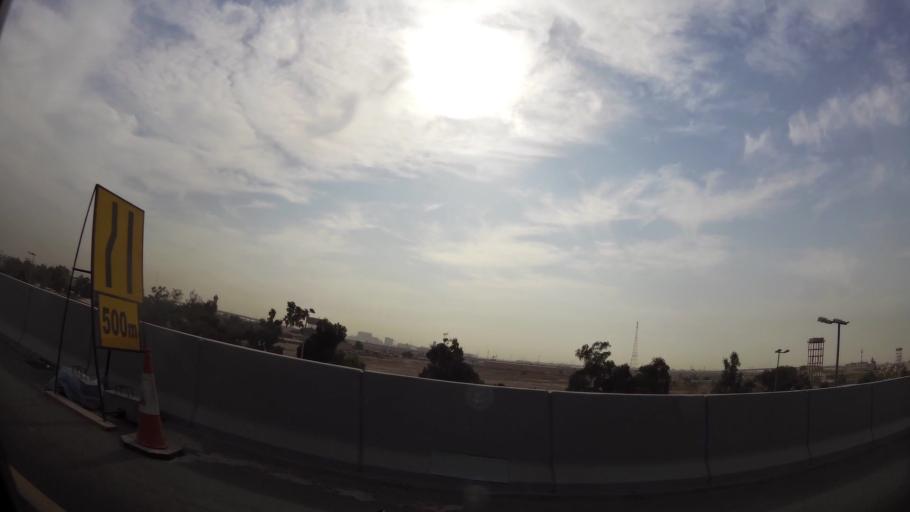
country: KW
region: Al Asimah
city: Ar Rabiyah
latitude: 29.3211
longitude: 47.8864
